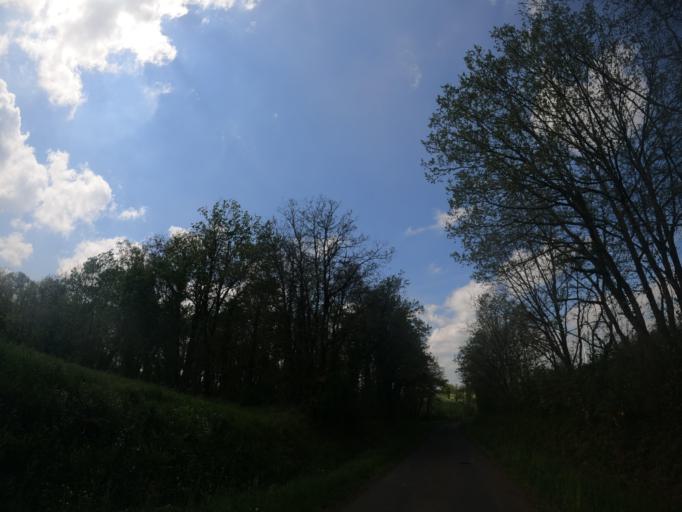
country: FR
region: Poitou-Charentes
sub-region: Departement des Deux-Sevres
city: Saint-Varent
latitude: 46.8591
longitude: -0.2135
